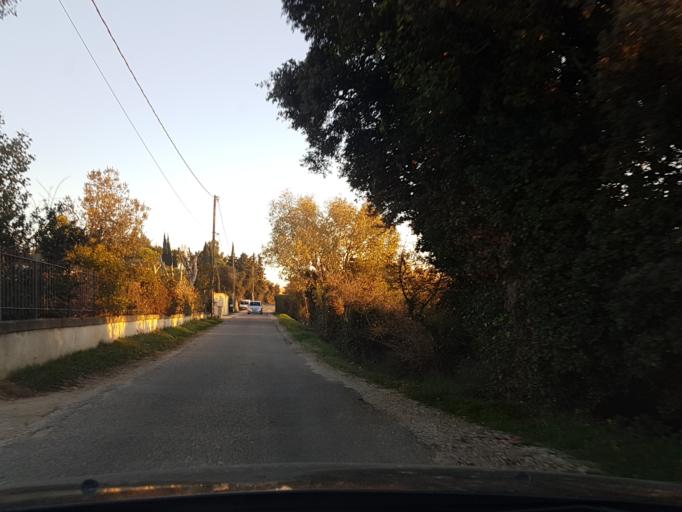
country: FR
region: Provence-Alpes-Cote d'Azur
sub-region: Departement du Vaucluse
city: Saint-Saturnin-les-Avignon
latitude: 43.9565
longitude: 4.9164
